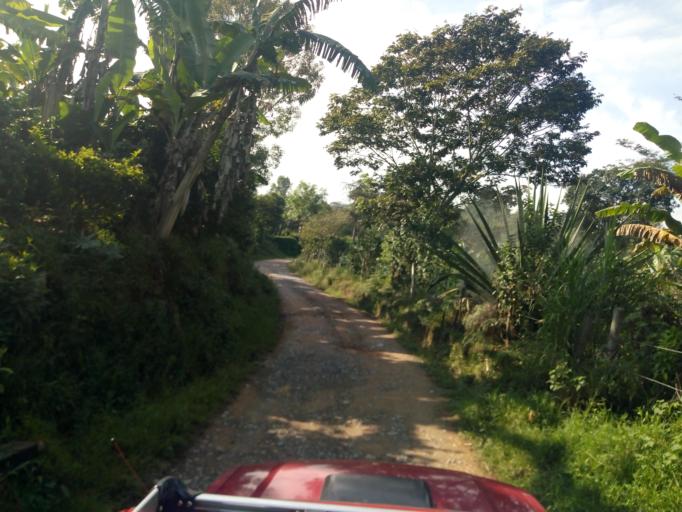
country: CO
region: Boyaca
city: Moniquira
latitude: 5.8879
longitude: -73.5239
